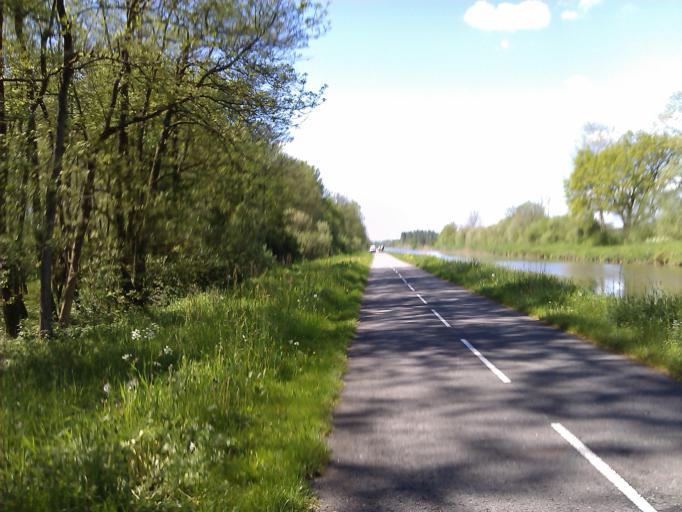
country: FR
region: Franche-Comte
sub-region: Territoire de Belfort
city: Montreux-Chateau
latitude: 47.5903
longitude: 6.9787
